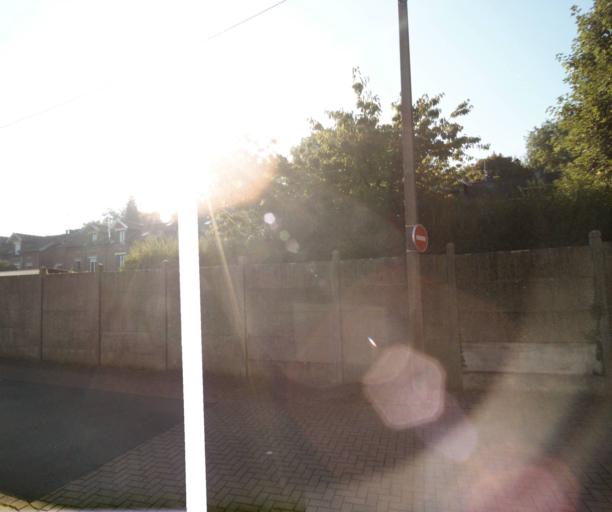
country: FR
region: Nord-Pas-de-Calais
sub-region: Departement du Nord
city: Lezennes
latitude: 50.6254
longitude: 3.1073
